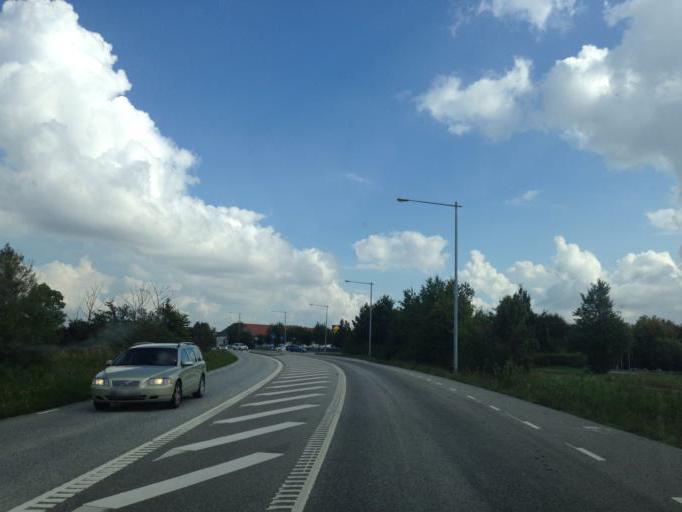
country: SE
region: Skane
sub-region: Lomma Kommun
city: Lomma
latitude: 55.6827
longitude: 13.0822
